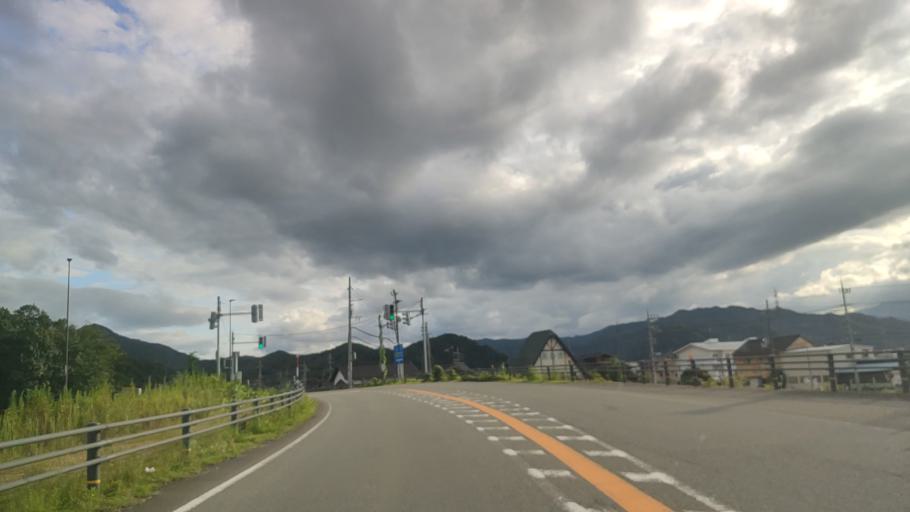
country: JP
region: Hyogo
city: Toyooka
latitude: 35.4780
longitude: 134.7866
